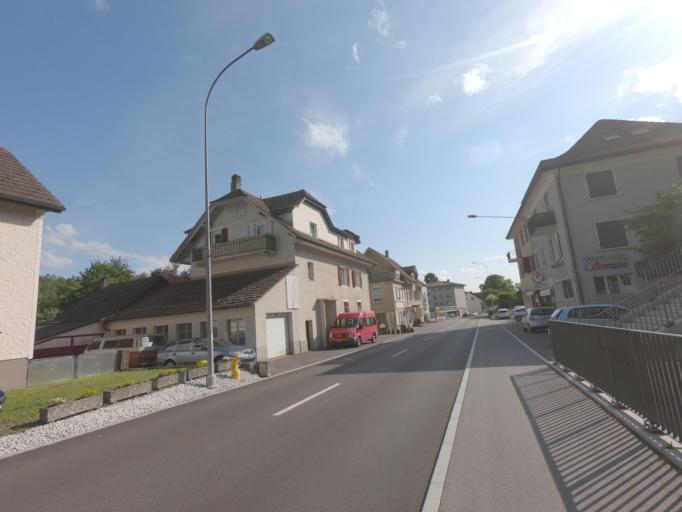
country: CH
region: Solothurn
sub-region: Bezirk Lebern
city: Langendorf
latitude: 47.2318
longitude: 7.5326
